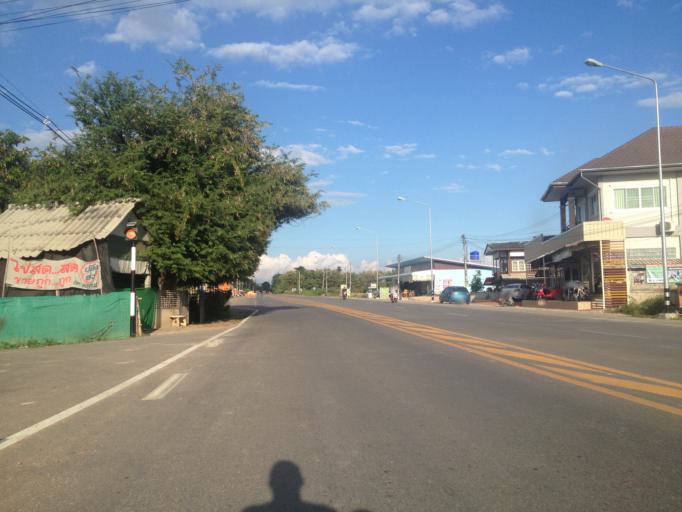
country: TH
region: Chiang Mai
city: San Pa Tong
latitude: 18.6073
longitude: 98.8382
